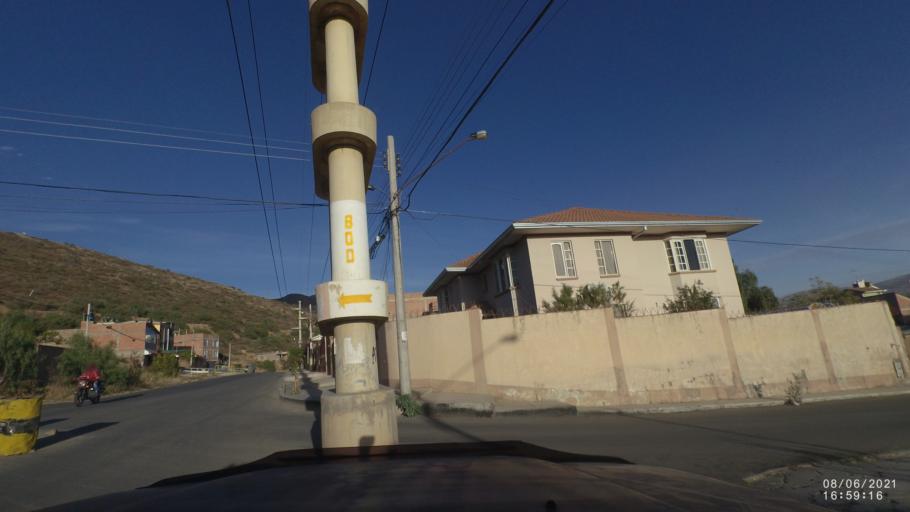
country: BO
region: Cochabamba
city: Cochabamba
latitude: -17.4166
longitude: -66.1243
